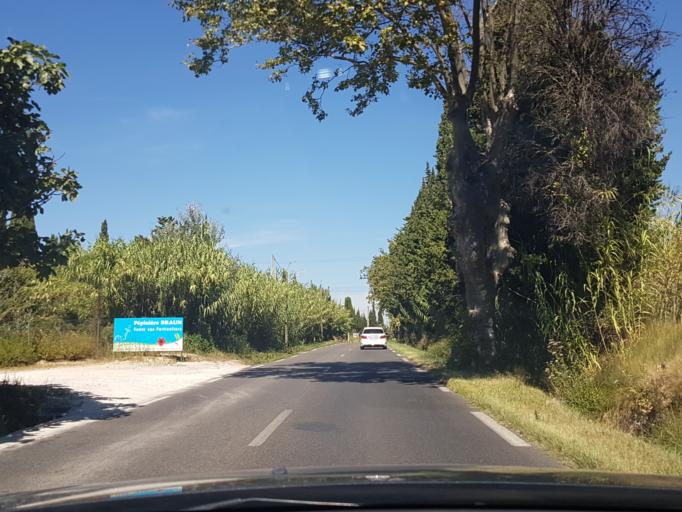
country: FR
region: Provence-Alpes-Cote d'Azur
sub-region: Departement des Bouches-du-Rhone
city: Eyragues
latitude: 43.8280
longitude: 4.8358
